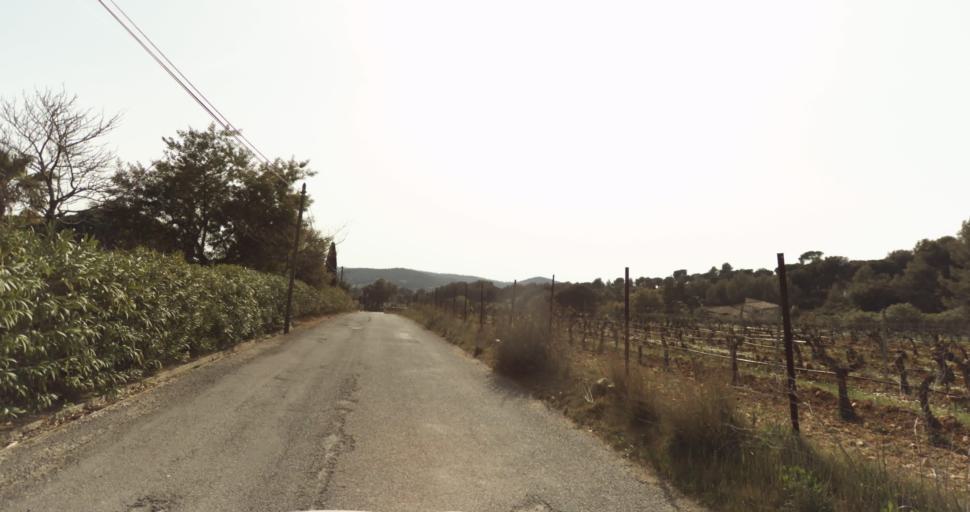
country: FR
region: Provence-Alpes-Cote d'Azur
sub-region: Departement du Var
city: Bormes-les-Mimosas
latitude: 43.1490
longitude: 6.3247
